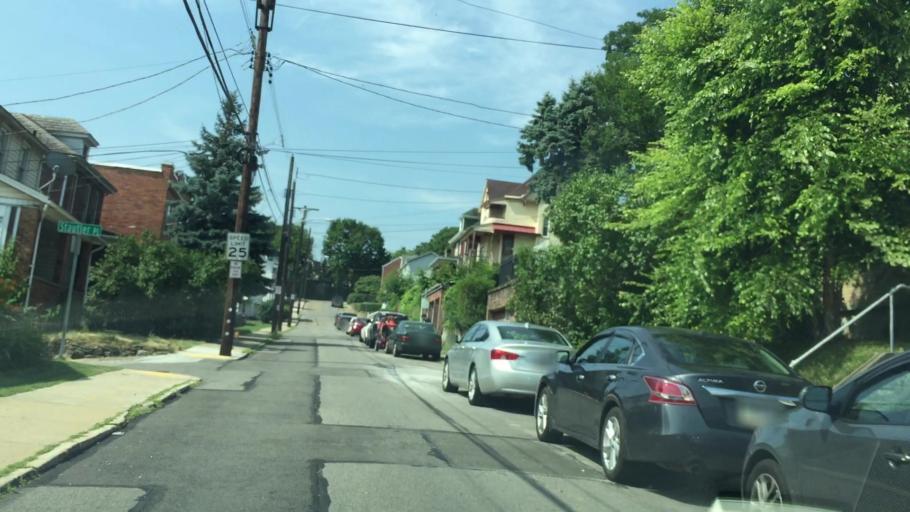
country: US
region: Pennsylvania
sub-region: Allegheny County
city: Carnegie
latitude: 40.4141
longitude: -80.0869
